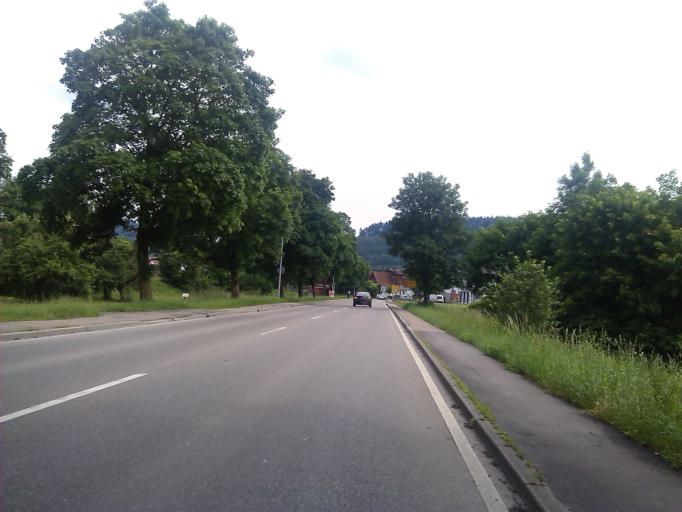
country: DE
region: Baden-Wuerttemberg
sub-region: Regierungsbezirk Stuttgart
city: Gaildorf
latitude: 48.9824
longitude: 9.7758
